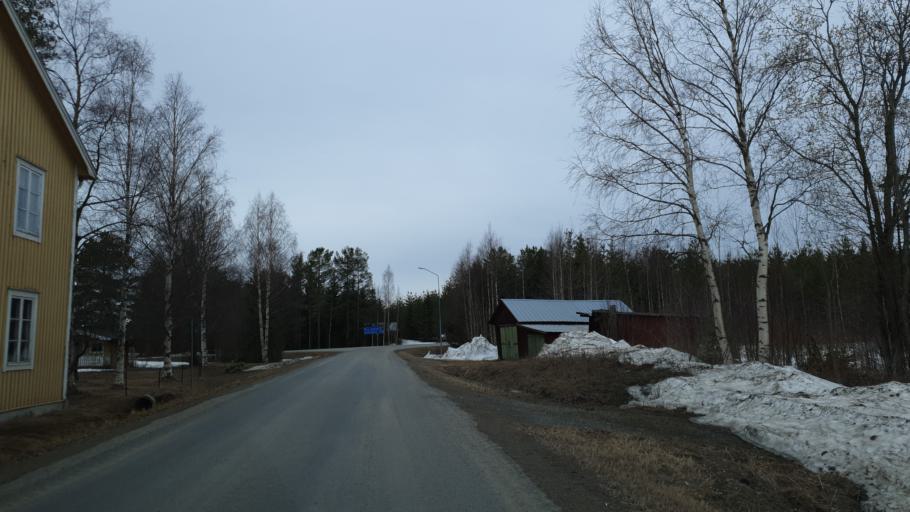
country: SE
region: Vaesterbotten
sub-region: Robertsfors Kommun
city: Robertsfors
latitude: 64.3770
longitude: 20.9044
